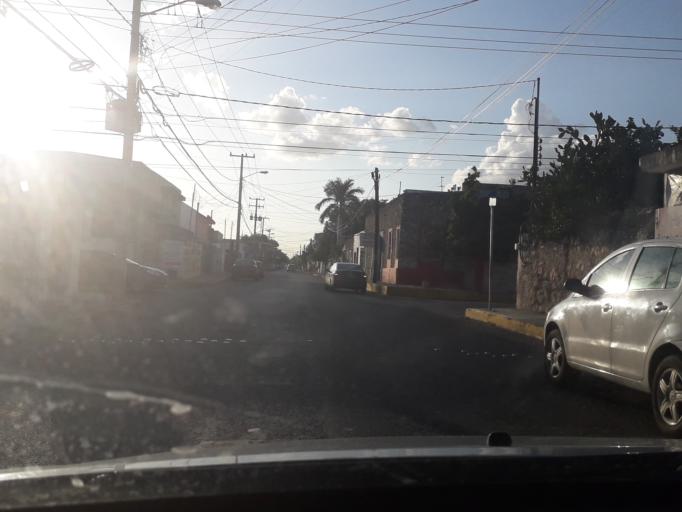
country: MX
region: Yucatan
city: Merida
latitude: 20.9722
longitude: -89.6459
